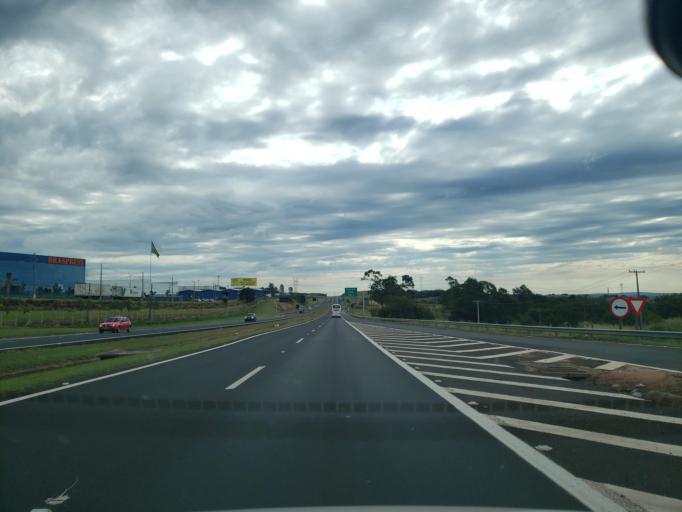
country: BR
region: Sao Paulo
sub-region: Bauru
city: Bauru
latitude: -22.2795
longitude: -49.0890
